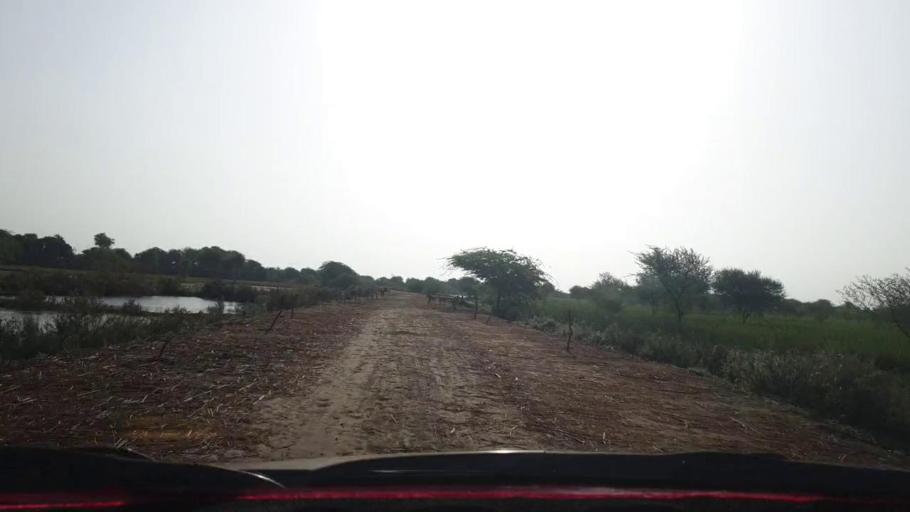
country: PK
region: Sindh
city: Talhar
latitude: 24.9297
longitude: 68.7611
